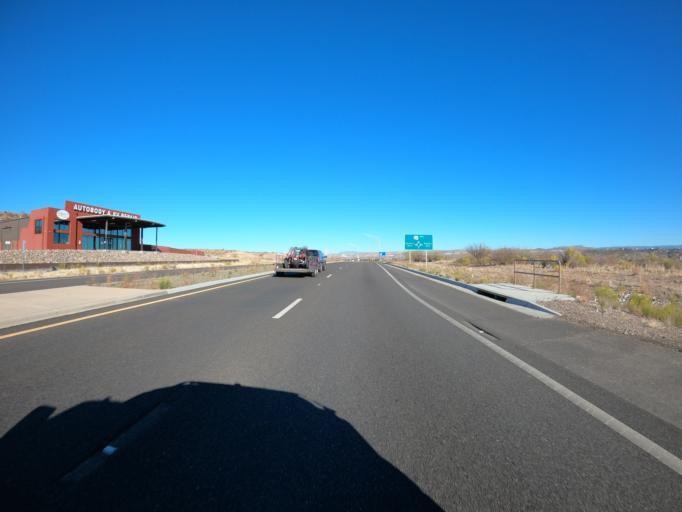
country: US
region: Arizona
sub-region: Yavapai County
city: Camp Verde
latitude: 34.5826
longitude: -111.8854
